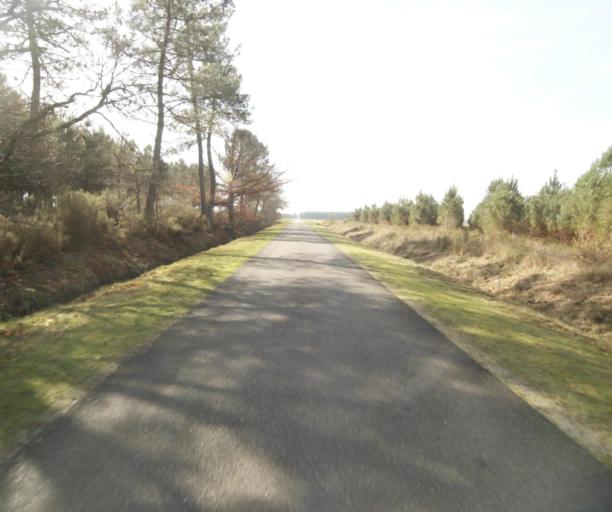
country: FR
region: Aquitaine
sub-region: Departement de la Gironde
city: Grignols
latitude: 44.1927
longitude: -0.1427
